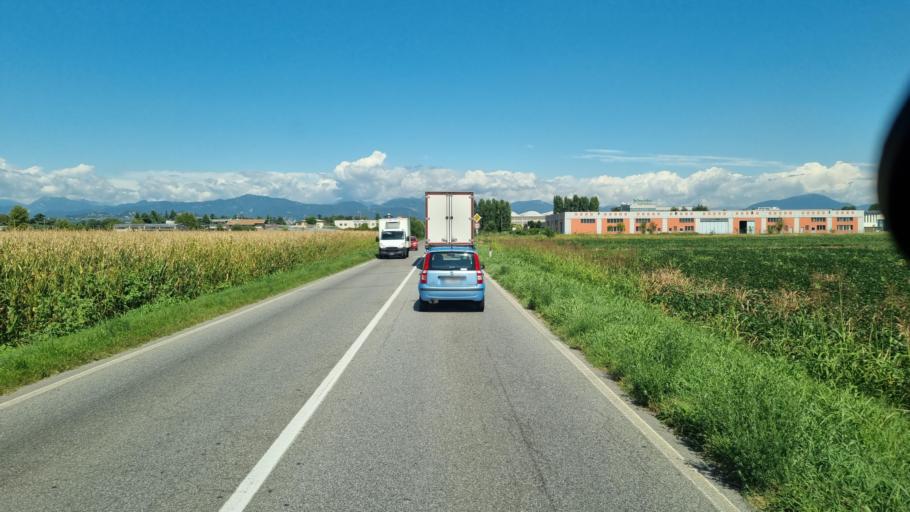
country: IT
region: Lombardy
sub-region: Provincia di Bergamo
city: Stezzano
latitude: 45.6392
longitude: 9.6464
